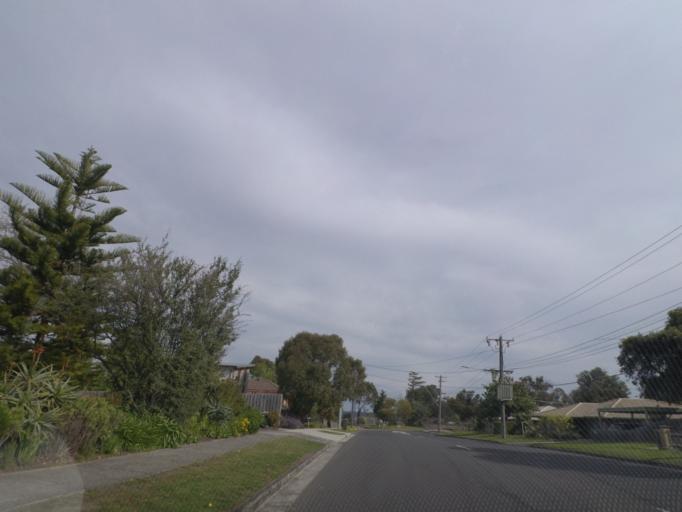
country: AU
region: Victoria
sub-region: Whitehorse
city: Vermont
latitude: -37.8467
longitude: 145.1990
